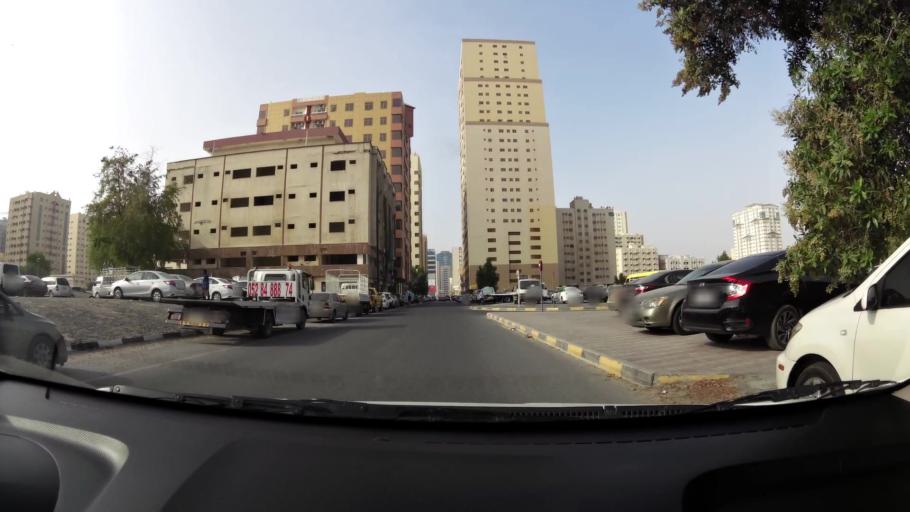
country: AE
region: Ash Shariqah
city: Sharjah
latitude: 25.3399
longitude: 55.3971
